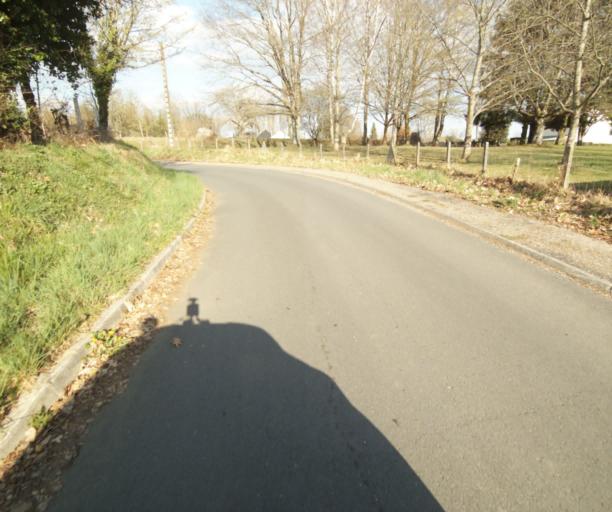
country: FR
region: Limousin
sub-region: Departement de la Correze
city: Saint-Clement
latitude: 45.3472
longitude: 1.6378
